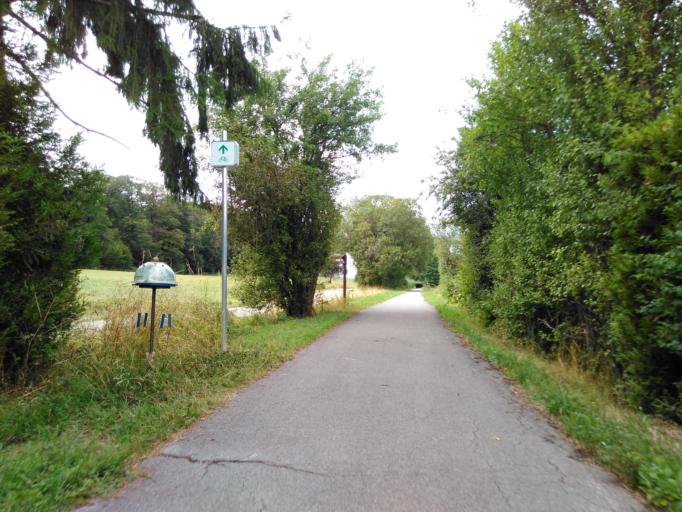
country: LU
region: Grevenmacher
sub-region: Canton d'Echternach
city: Consdorf
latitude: 49.7629
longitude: 6.3463
